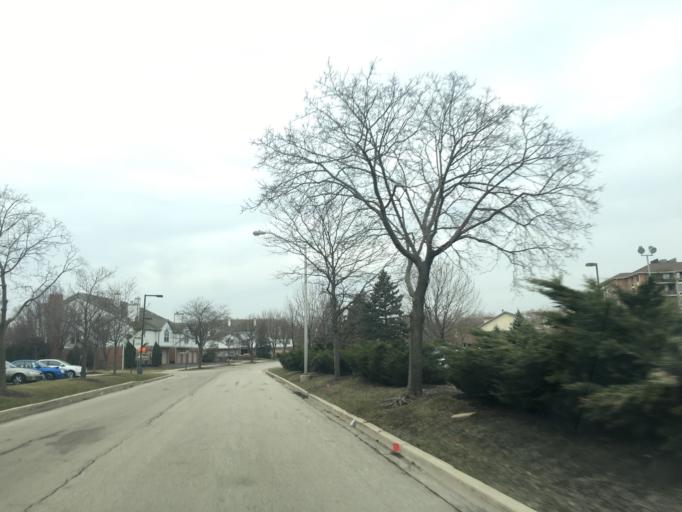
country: US
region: Illinois
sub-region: Cook County
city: Hoffman Estates
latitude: 42.0580
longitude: -88.0812
